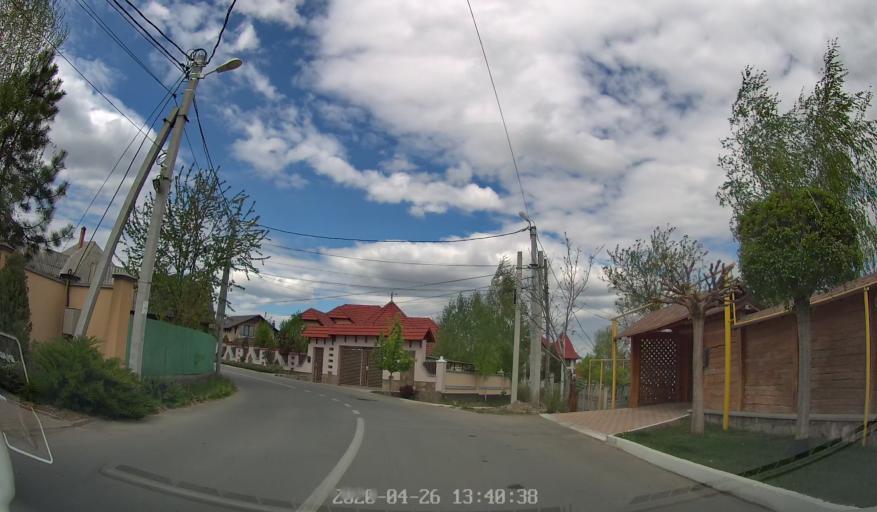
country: MD
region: Criuleni
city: Criuleni
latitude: 47.2159
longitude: 29.1656
